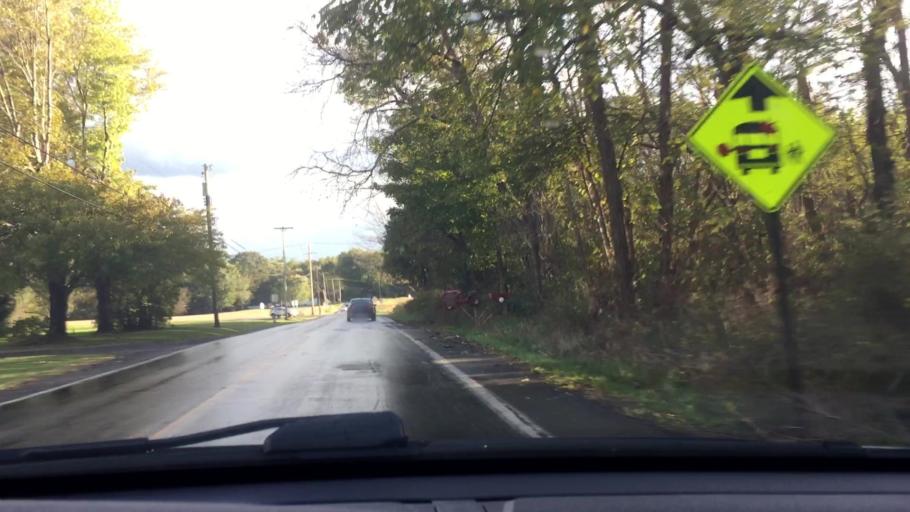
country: US
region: Pennsylvania
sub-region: Lawrence County
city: Oakwood
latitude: 41.0302
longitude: -80.4422
